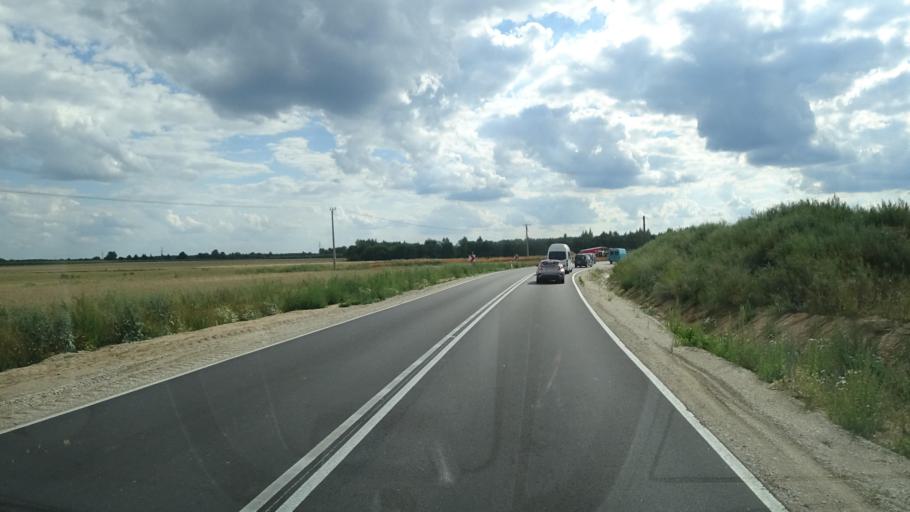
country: PL
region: Masovian Voivodeship
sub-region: Powiat ostrowski
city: Ostrow Mazowiecka
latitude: 52.8188
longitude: 21.9220
